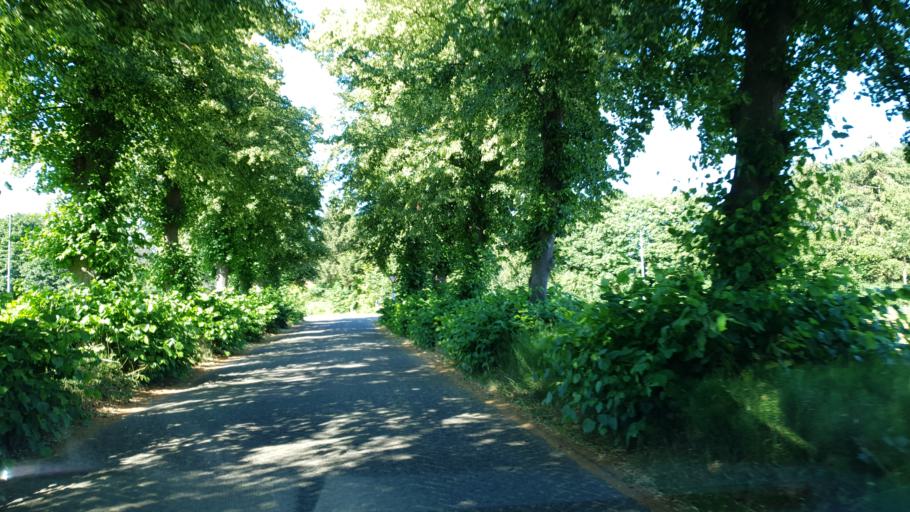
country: BE
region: Flanders
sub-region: Provincie Antwerpen
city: Merksplas
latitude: 51.3789
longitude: 4.8284
